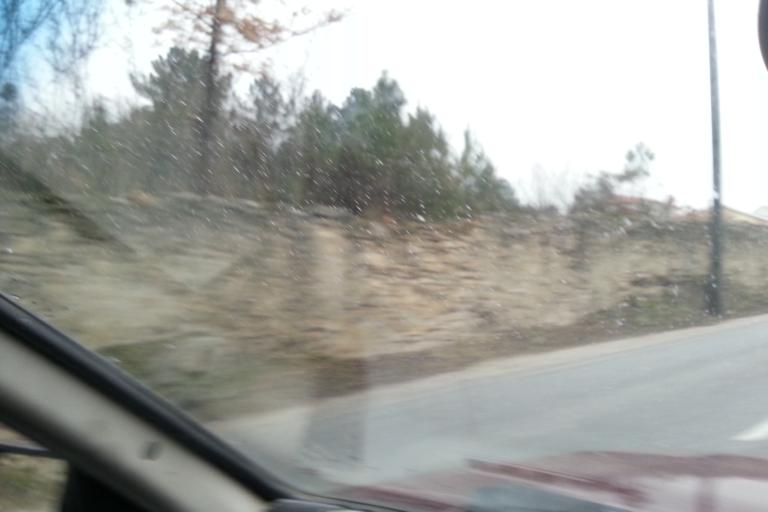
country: PT
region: Viseu
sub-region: Mangualde
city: Mangualde
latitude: 40.6058
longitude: -7.7440
